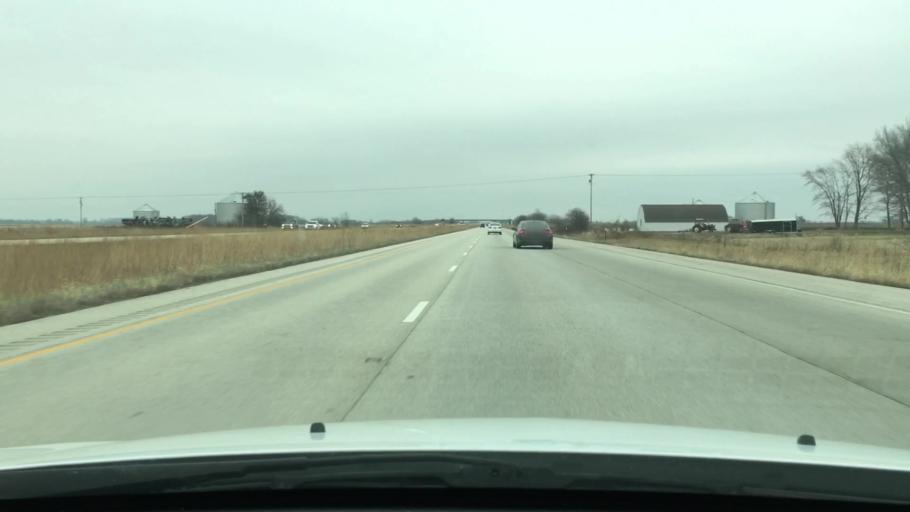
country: US
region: Illinois
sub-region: Sangamon County
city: New Berlin
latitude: 39.7401
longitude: -89.9173
